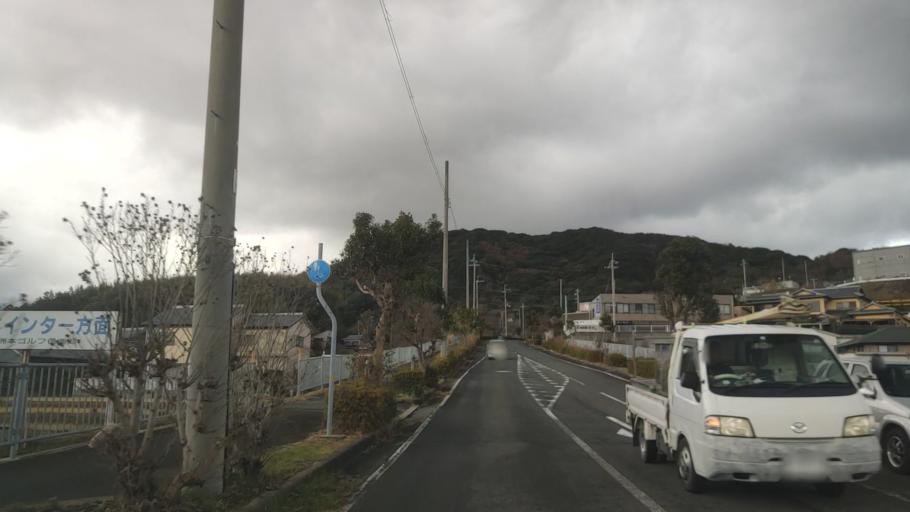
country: JP
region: Hyogo
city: Sumoto
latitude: 34.3332
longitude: 134.8687
